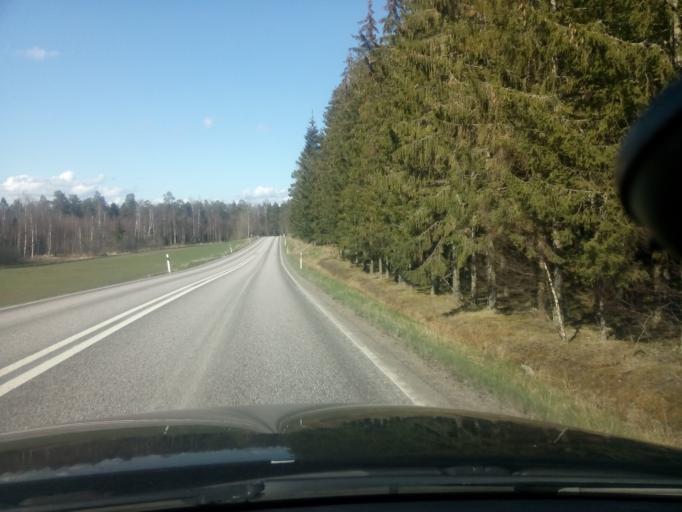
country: SE
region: Soedermanland
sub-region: Flens Kommun
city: Malmkoping
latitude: 59.0284
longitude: 16.8454
